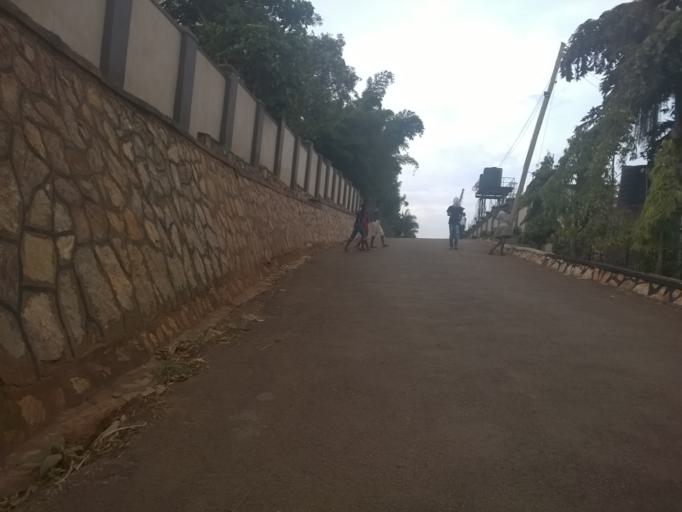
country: UG
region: Central Region
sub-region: Wakiso District
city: Kireka
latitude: 0.3220
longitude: 32.6388
